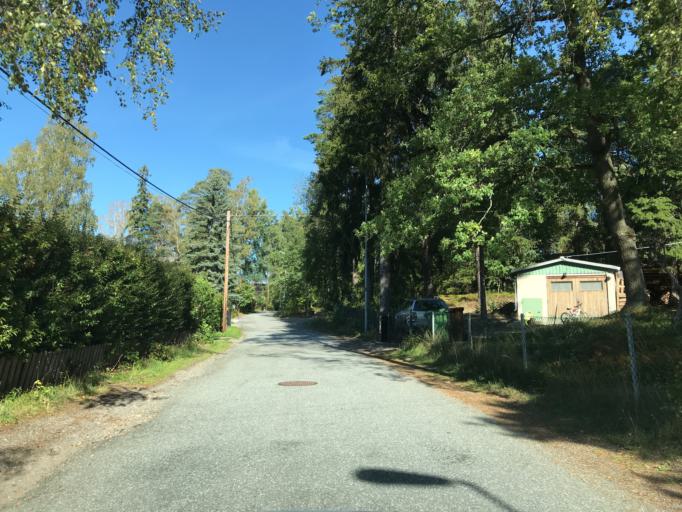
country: SE
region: Stockholm
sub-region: Sollentuna Kommun
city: Sollentuna
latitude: 59.4289
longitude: 17.9269
